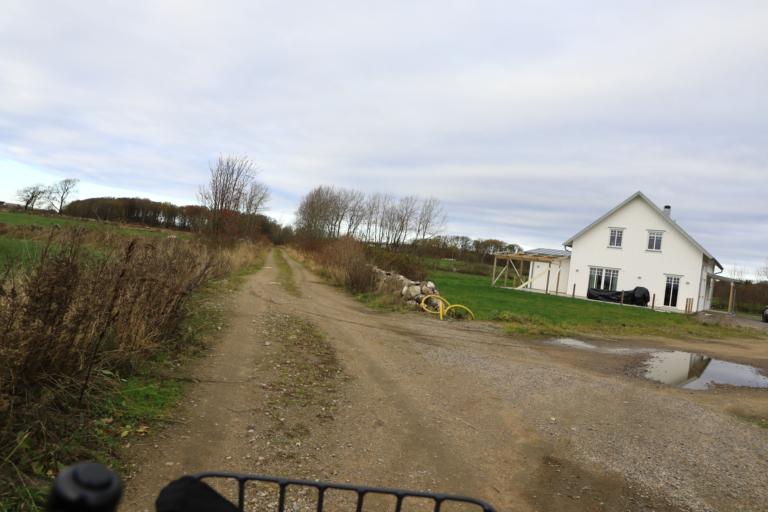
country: SE
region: Halland
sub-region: Varbergs Kommun
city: Traslovslage
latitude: 57.0577
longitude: 12.3343
